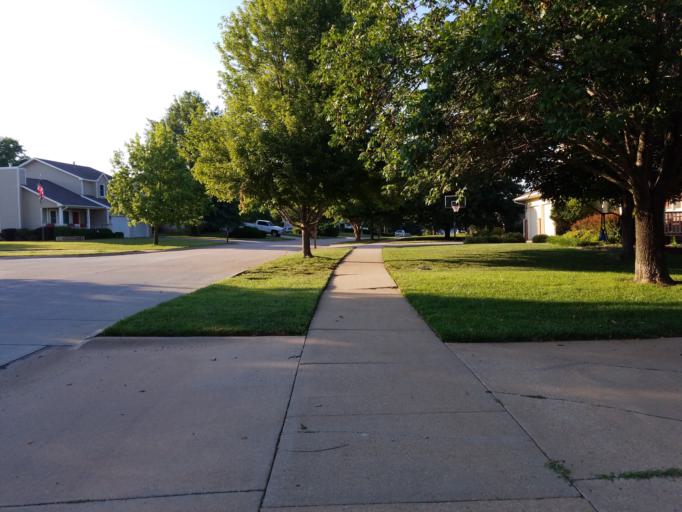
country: US
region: Kansas
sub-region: Riley County
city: Manhattan
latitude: 39.2114
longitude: -96.6207
